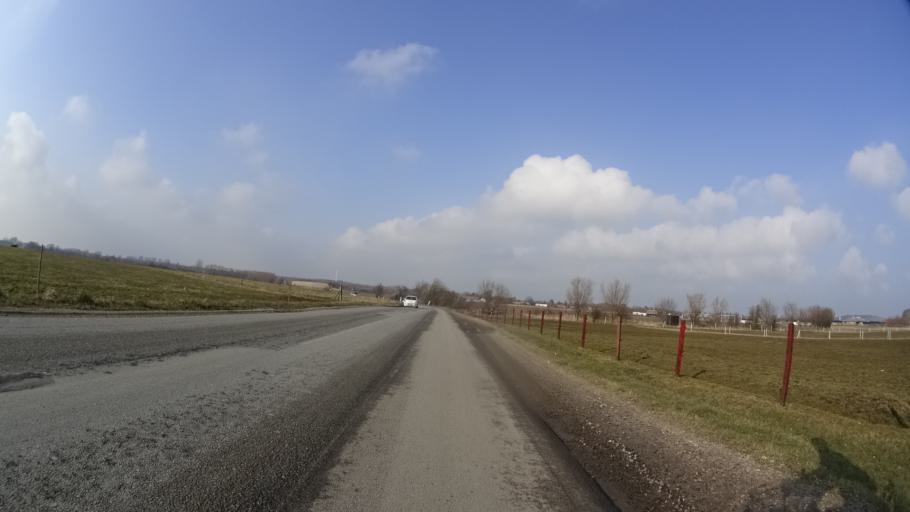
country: DK
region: Central Jutland
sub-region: Arhus Kommune
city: Tranbjerg
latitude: 56.0780
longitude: 10.1415
